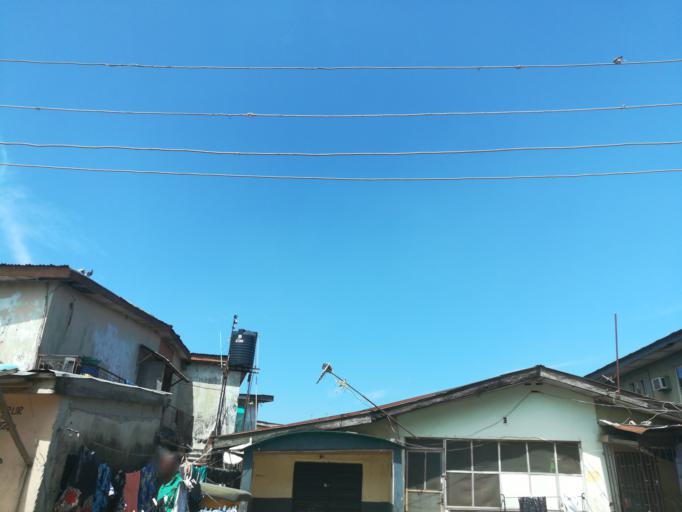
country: NG
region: Lagos
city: Oshodi
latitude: 6.5647
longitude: 3.3322
